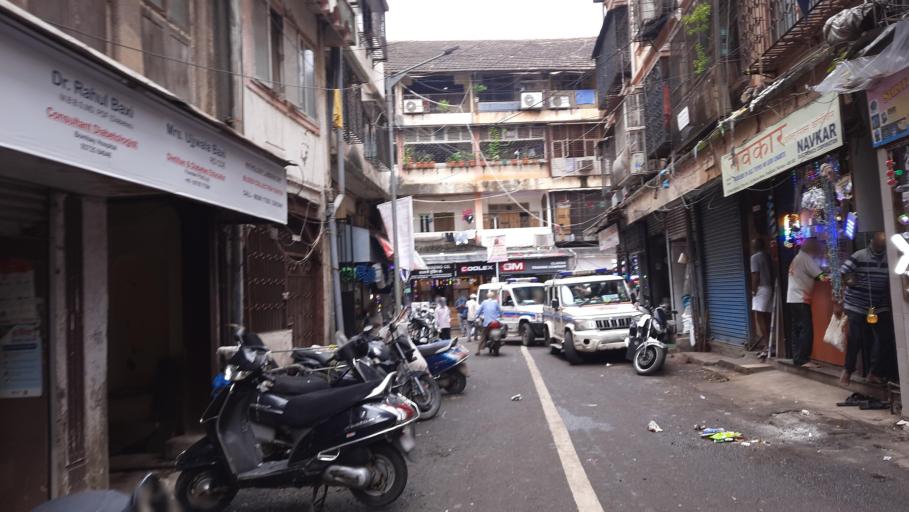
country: IN
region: Maharashtra
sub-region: Raigarh
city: Uran
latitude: 18.9435
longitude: 72.8269
